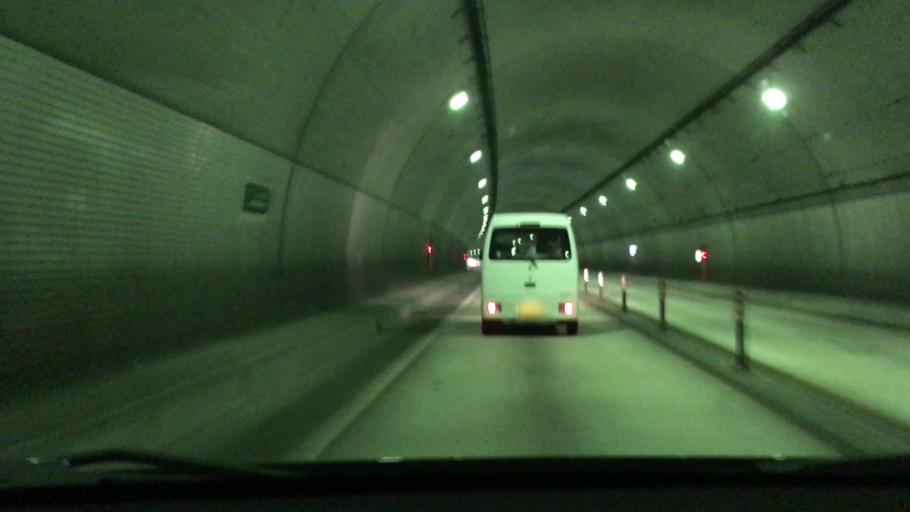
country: JP
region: Nagasaki
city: Sasebo
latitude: 33.0920
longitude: 129.7786
